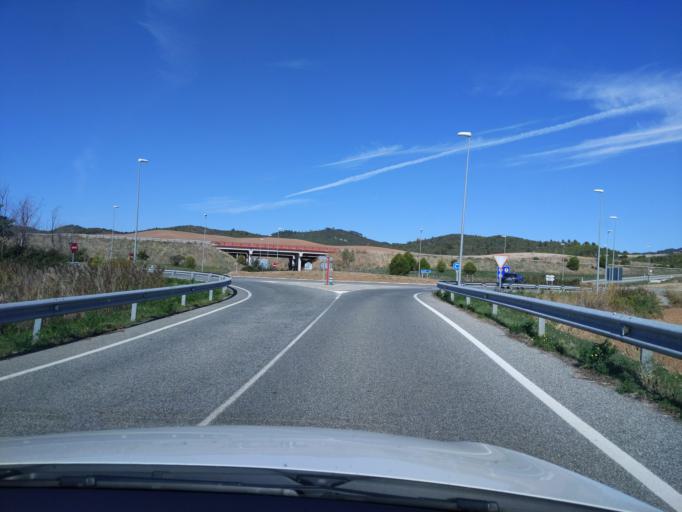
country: ES
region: Navarre
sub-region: Provincia de Navarra
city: Arroniz
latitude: 42.5993
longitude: -2.1188
